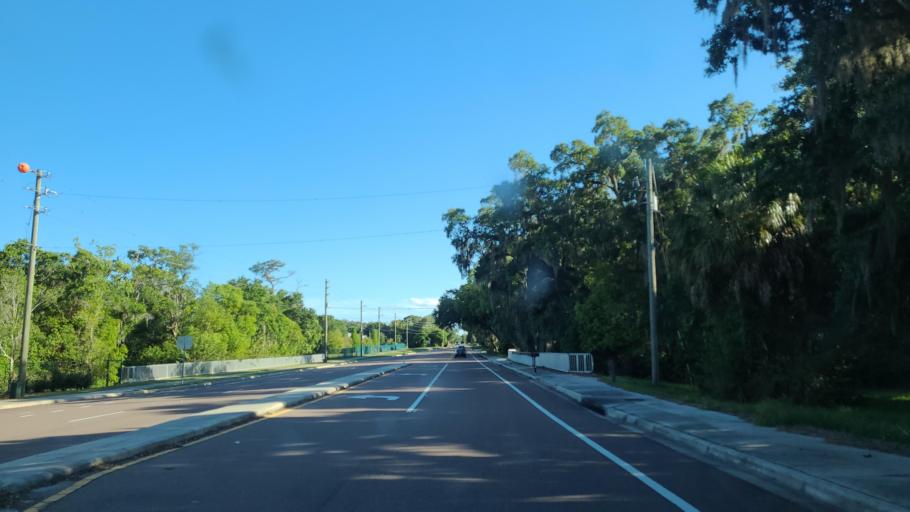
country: US
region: Florida
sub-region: Hillsborough County
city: Apollo Beach
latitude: 27.7874
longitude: -82.3474
